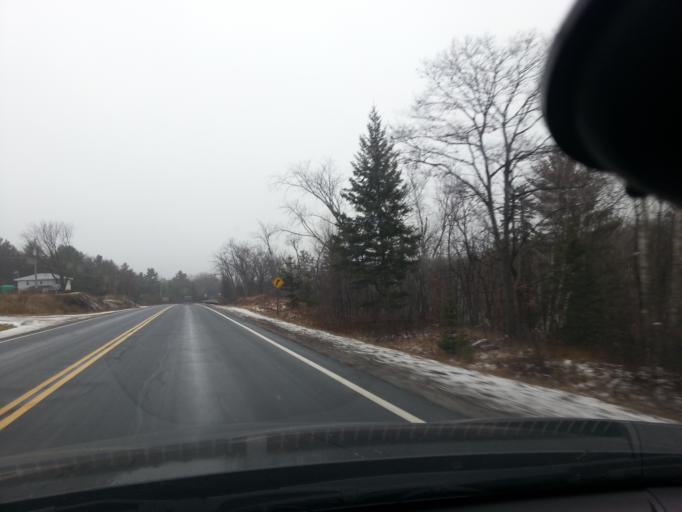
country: CA
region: Ontario
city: Greater Napanee
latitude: 44.6405
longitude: -77.1320
